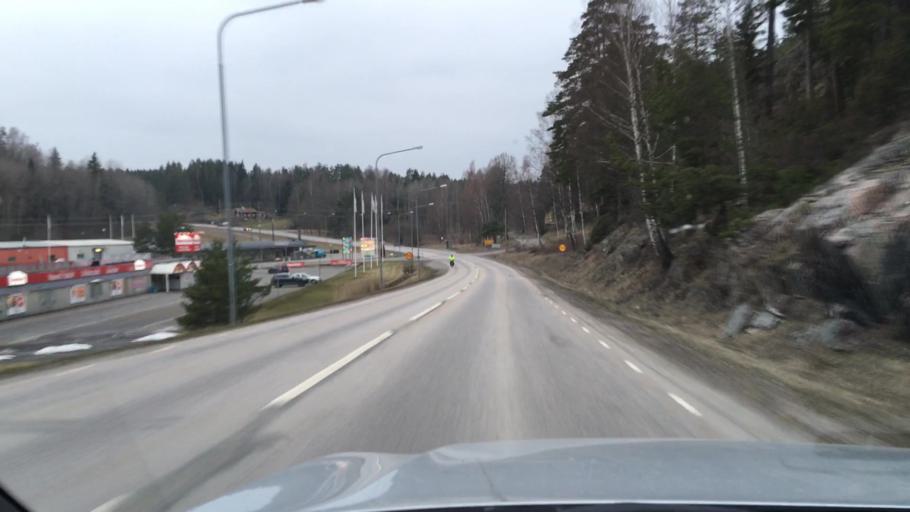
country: SE
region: OEstergoetland
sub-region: Valdemarsviks Kommun
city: Valdemarsvik
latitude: 58.2160
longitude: 16.5794
